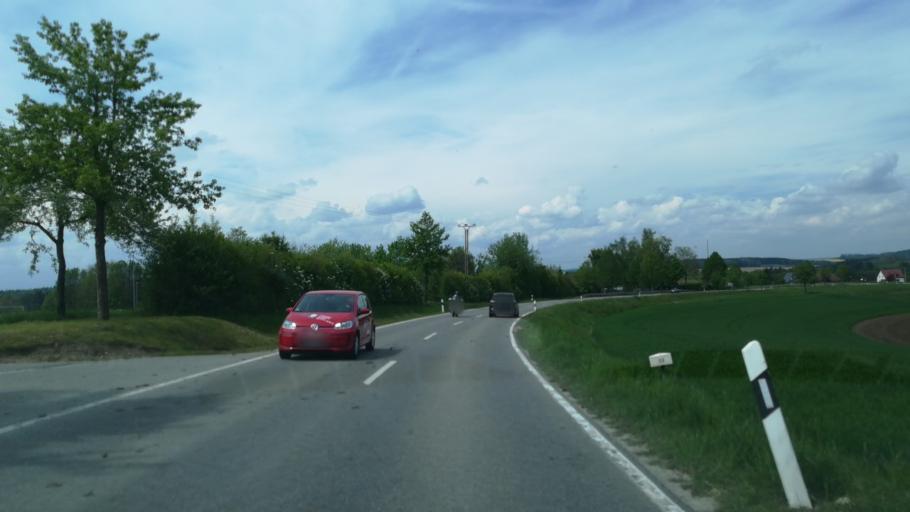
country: DE
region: Baden-Wuerttemberg
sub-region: Freiburg Region
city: Muhlingen
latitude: 47.8892
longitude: 9.0353
